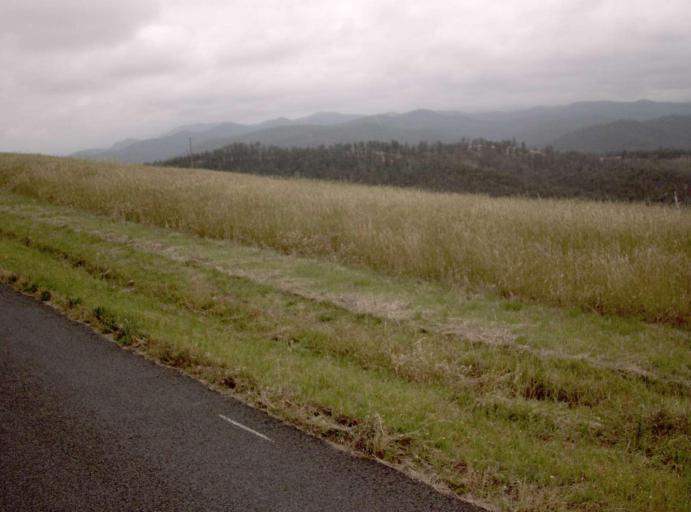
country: AU
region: Victoria
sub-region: Wellington
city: Heyfield
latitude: -37.8375
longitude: 146.6831
